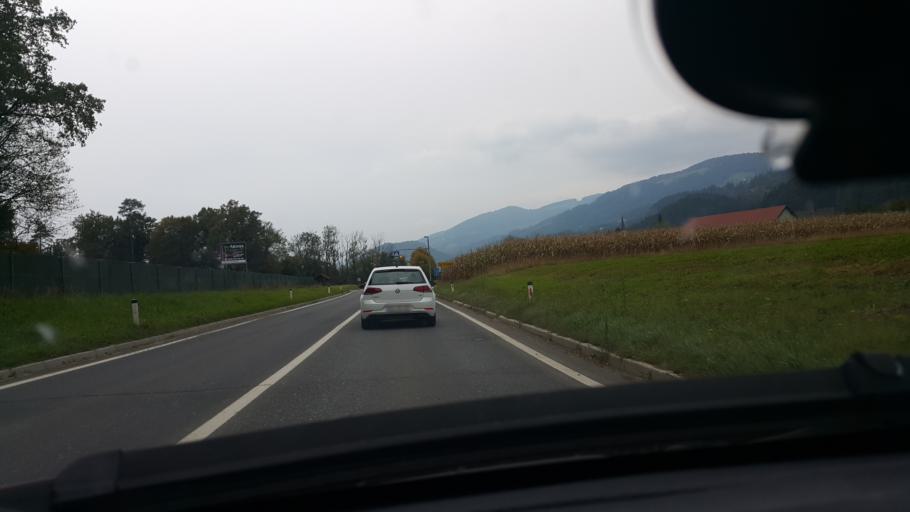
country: SI
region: Radlje ob Dravi
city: Radlje ob Dravi
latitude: 46.6142
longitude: 15.2034
